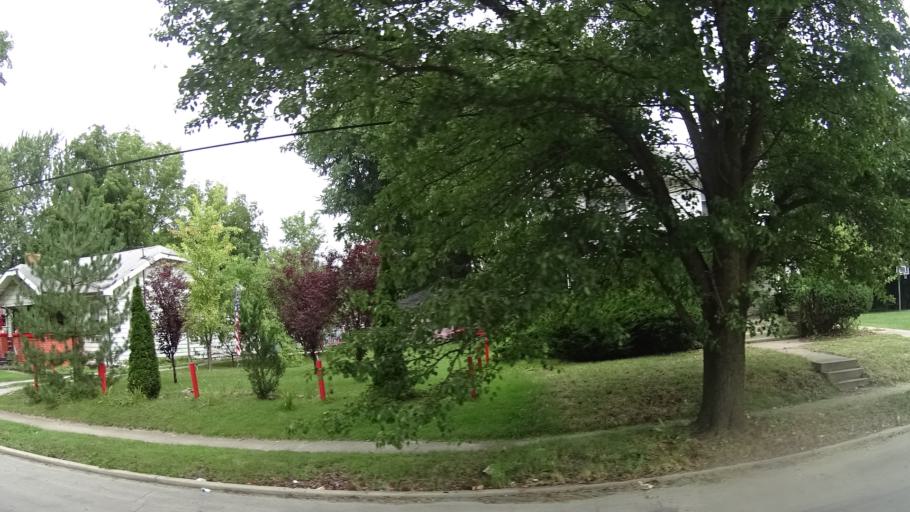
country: US
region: Indiana
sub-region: Madison County
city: Anderson
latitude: 40.1027
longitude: -85.7051
